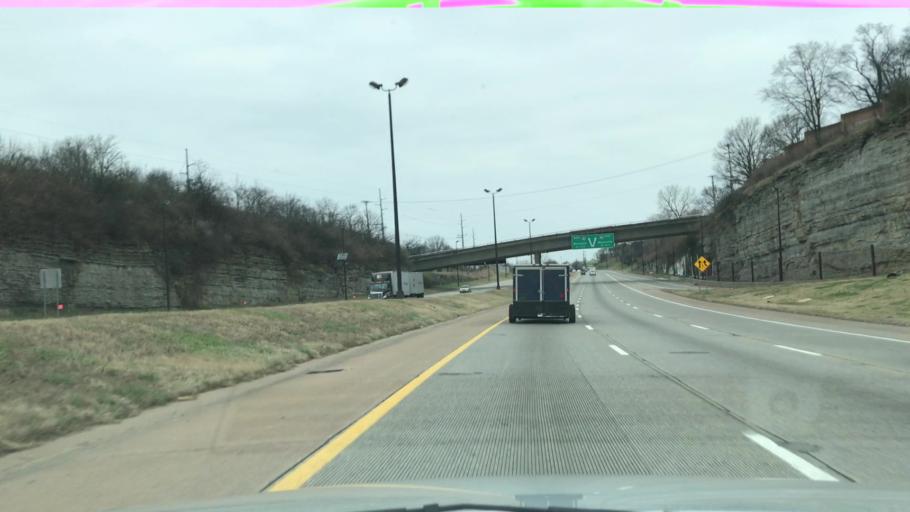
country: US
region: Tennessee
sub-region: Davidson County
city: Nashville
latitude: 36.1412
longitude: -86.8229
